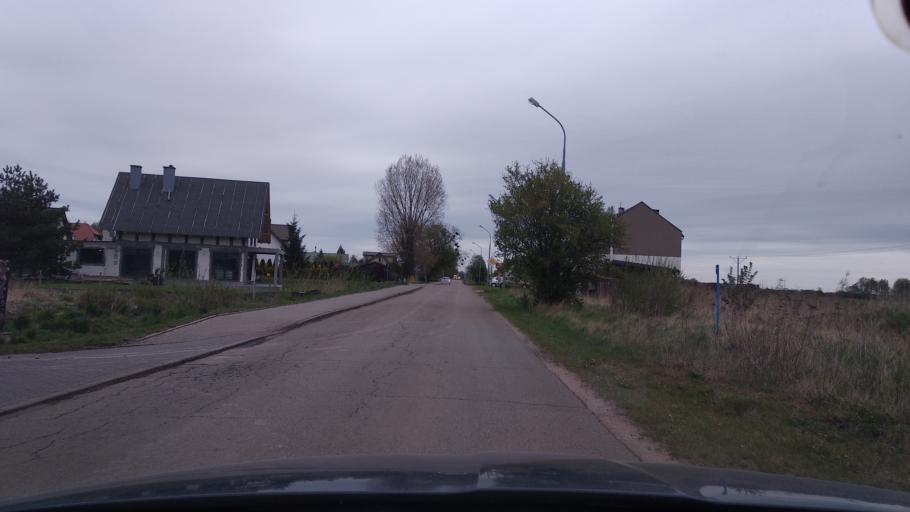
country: PL
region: Pomeranian Voivodeship
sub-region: Powiat gdanski
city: Pruszcz Gdanski
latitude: 54.2781
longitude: 18.6550
